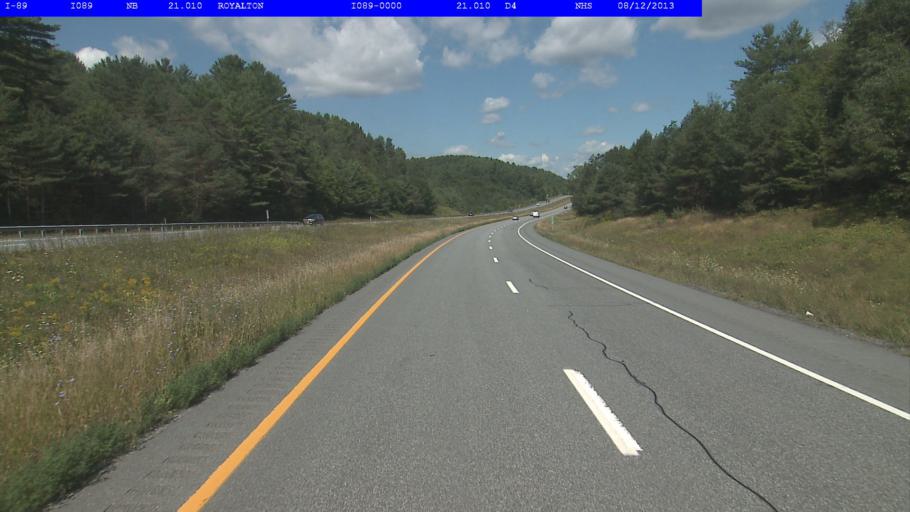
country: US
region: Vermont
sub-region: Orange County
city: Randolph
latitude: 43.8132
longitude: -72.5645
